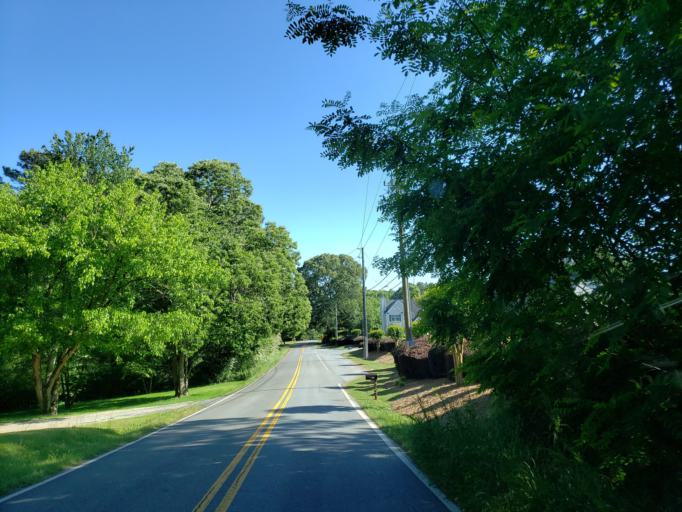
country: US
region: Georgia
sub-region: Paulding County
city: Hiram
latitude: 33.9091
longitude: -84.7936
